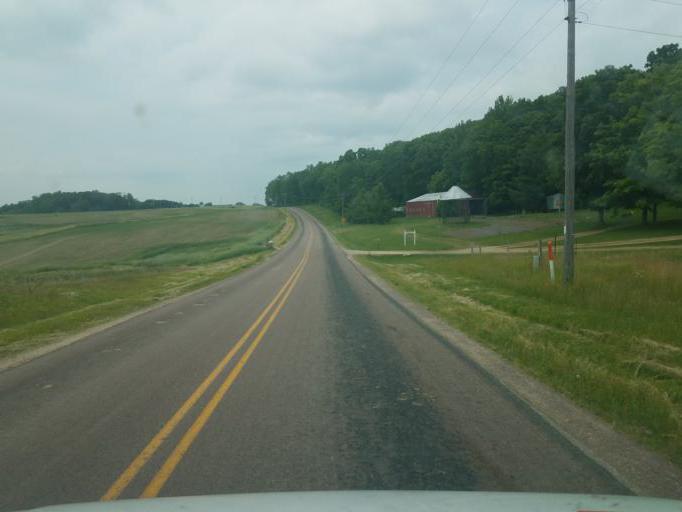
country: US
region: Wisconsin
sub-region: Vernon County
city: Hillsboro
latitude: 43.5887
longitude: -90.3738
